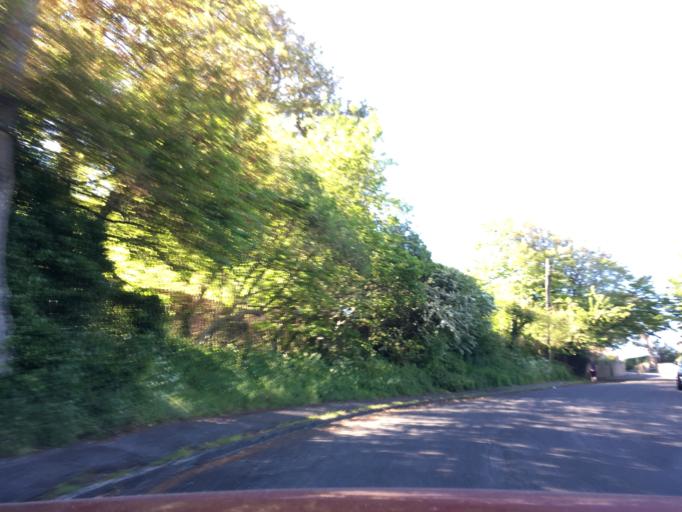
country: GB
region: England
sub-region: North Somerset
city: Portishead
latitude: 51.4934
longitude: -2.7685
